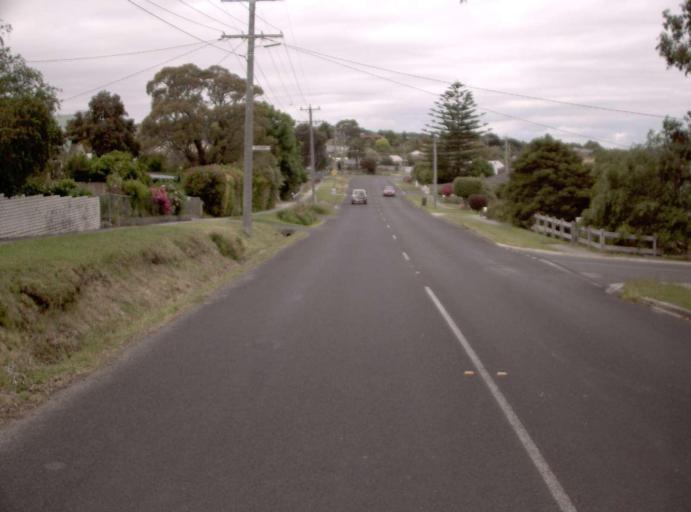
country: AU
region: Victoria
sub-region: Bass Coast
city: North Wonthaggi
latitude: -38.4366
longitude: 145.8157
